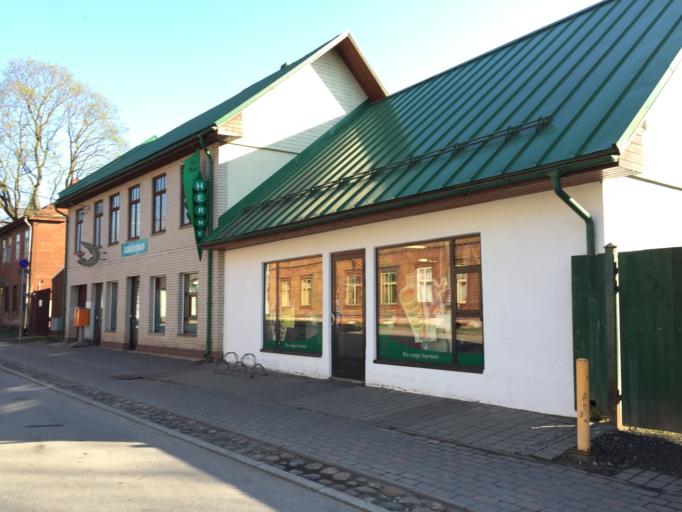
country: EE
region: Tartu
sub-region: Tartu linn
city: Tartu
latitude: 58.3850
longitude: 26.7167
